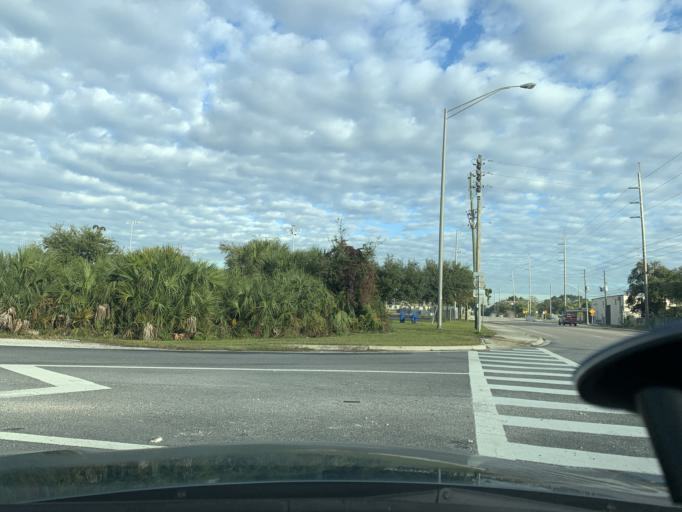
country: US
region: Florida
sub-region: Pinellas County
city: Saint Petersburg
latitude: 27.7606
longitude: -82.6754
